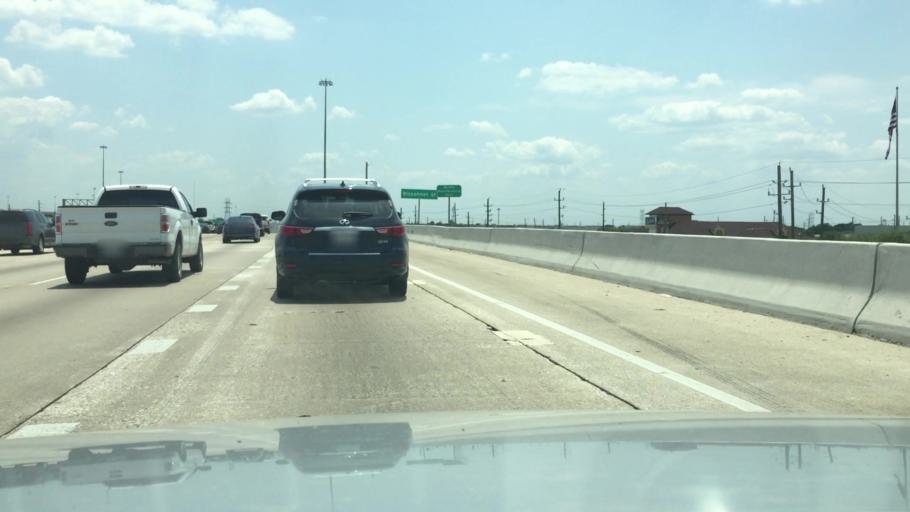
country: US
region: Texas
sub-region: Fort Bend County
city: Meadows Place
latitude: 29.6755
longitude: -95.5605
